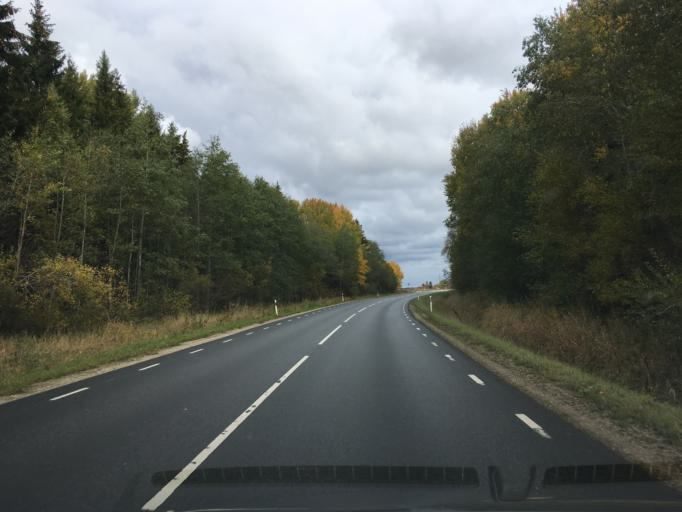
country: EE
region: Harju
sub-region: Anija vald
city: Kehra
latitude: 59.2717
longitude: 25.3569
